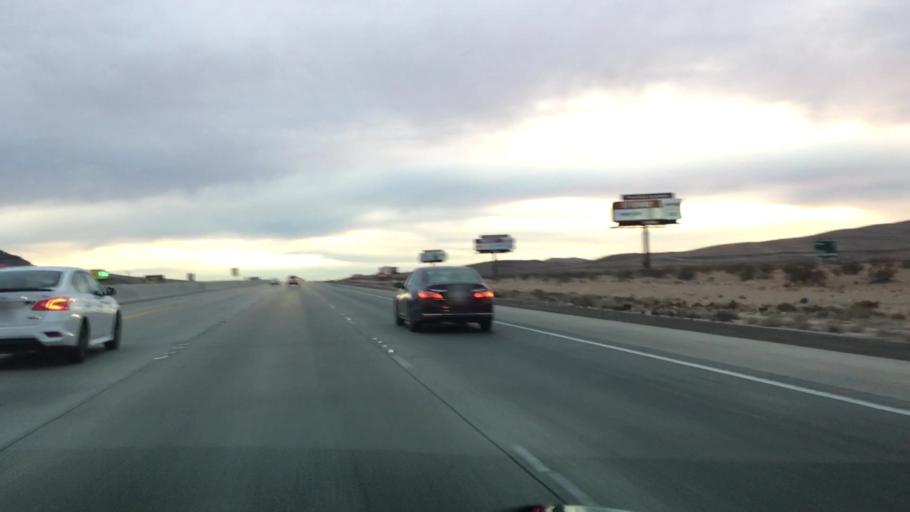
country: US
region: Nevada
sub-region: Clark County
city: Enterprise
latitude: 35.9231
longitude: -115.1999
